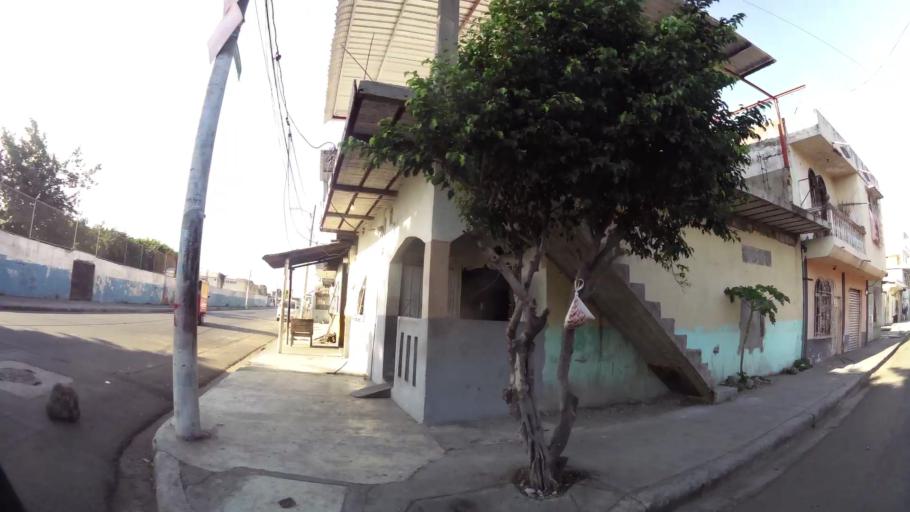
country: EC
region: Guayas
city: Guayaquil
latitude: -2.2243
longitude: -79.9276
